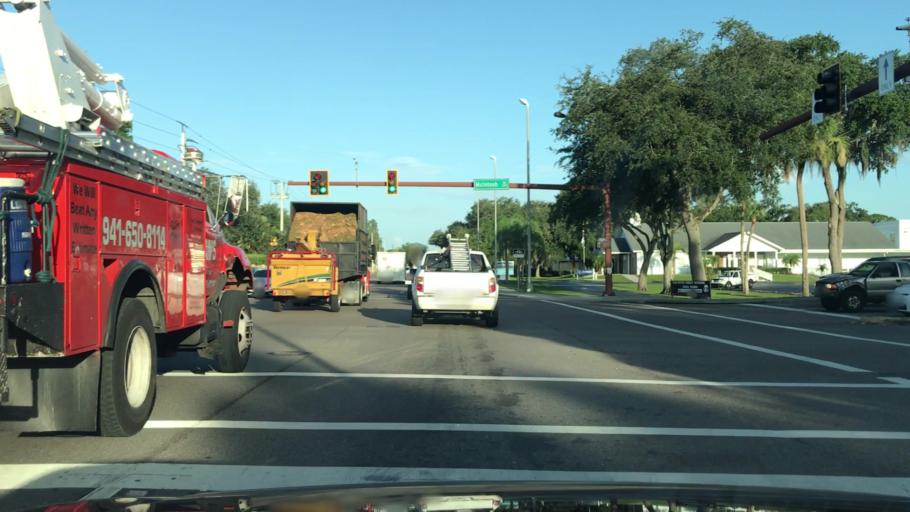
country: US
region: Florida
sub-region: Sarasota County
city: Sarasota Springs
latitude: 27.3231
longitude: -82.4826
